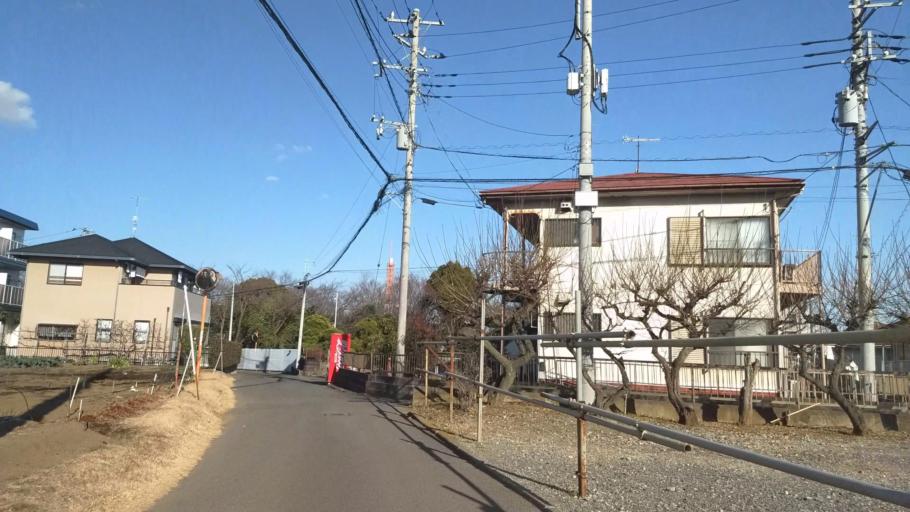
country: JP
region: Kanagawa
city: Isehara
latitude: 35.3642
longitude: 139.2704
